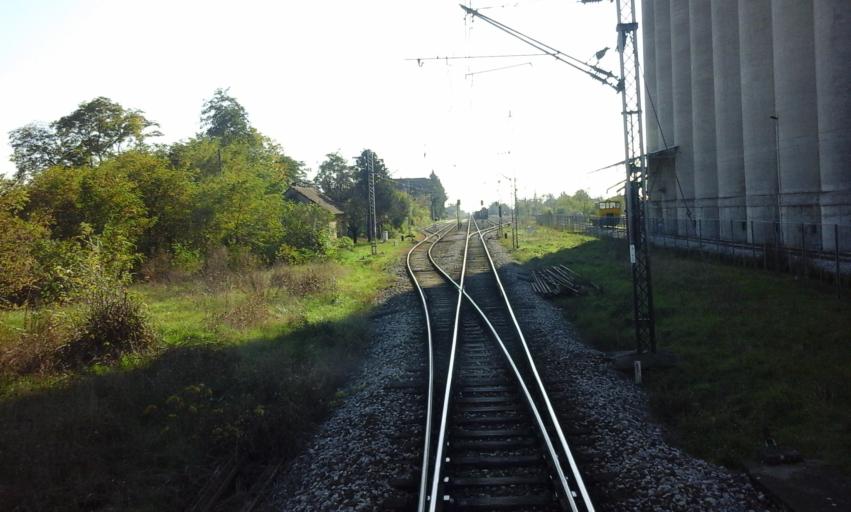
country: RS
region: Autonomna Pokrajina Vojvodina
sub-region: Severnobacki Okrug
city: Backa Topola
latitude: 45.9425
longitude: 19.6687
